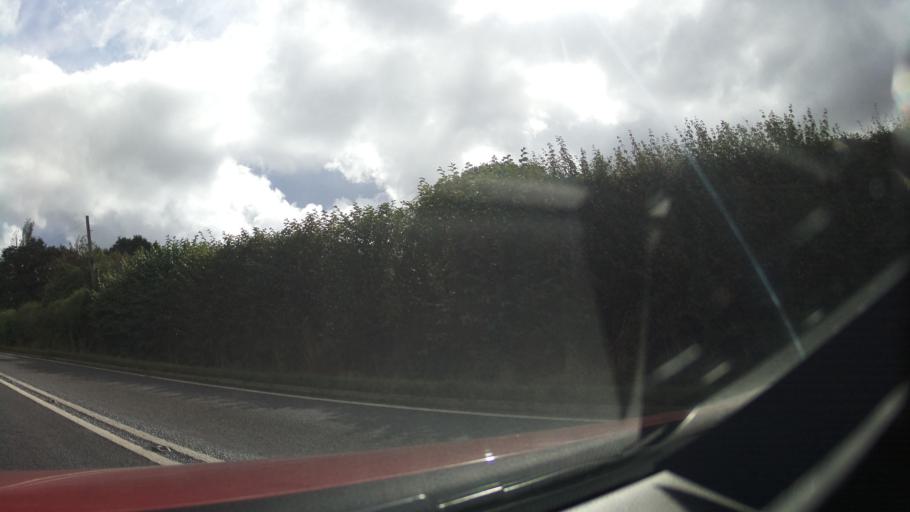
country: GB
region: England
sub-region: Shropshire
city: Bridgnorth
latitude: 52.5776
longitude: -2.3952
